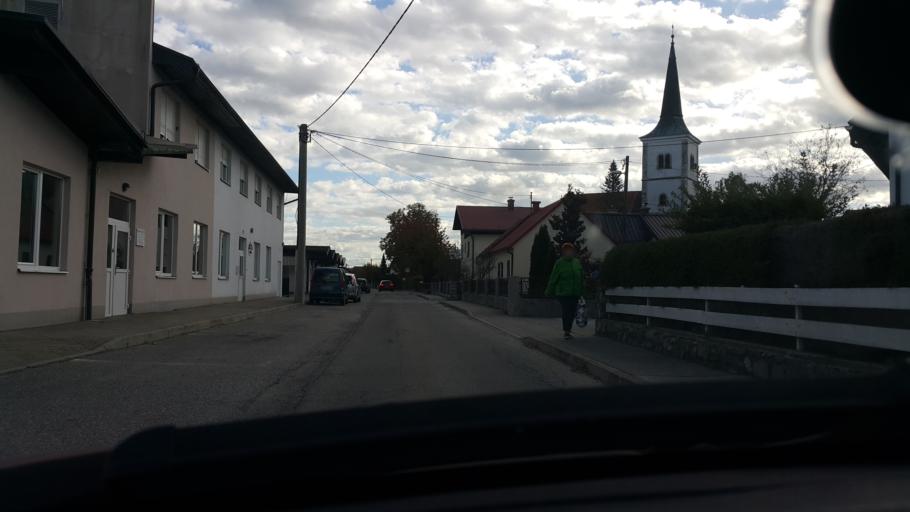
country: SI
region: Miklavz na Dravskem Polju
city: Miklavz na Dravskem Polju
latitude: 46.5369
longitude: 15.6878
